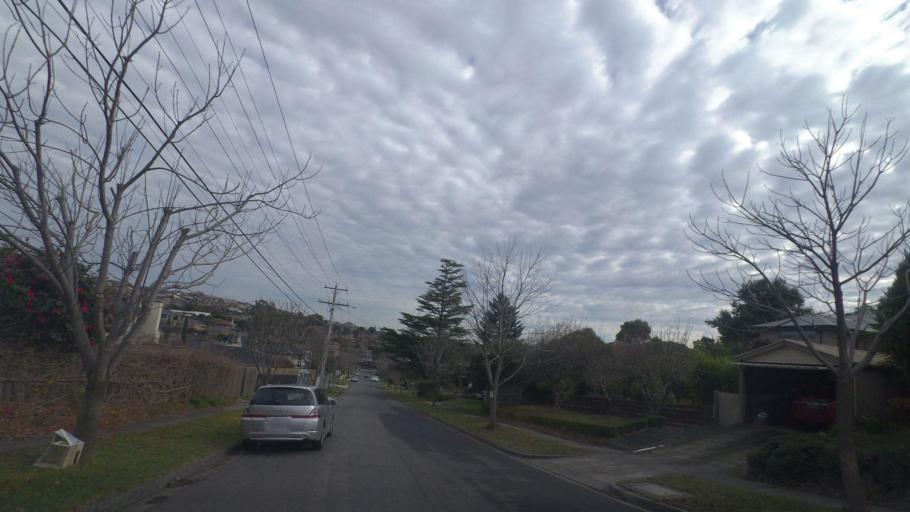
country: AU
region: Victoria
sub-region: Manningham
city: Templestowe Lower
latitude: -37.7650
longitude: 145.1033
